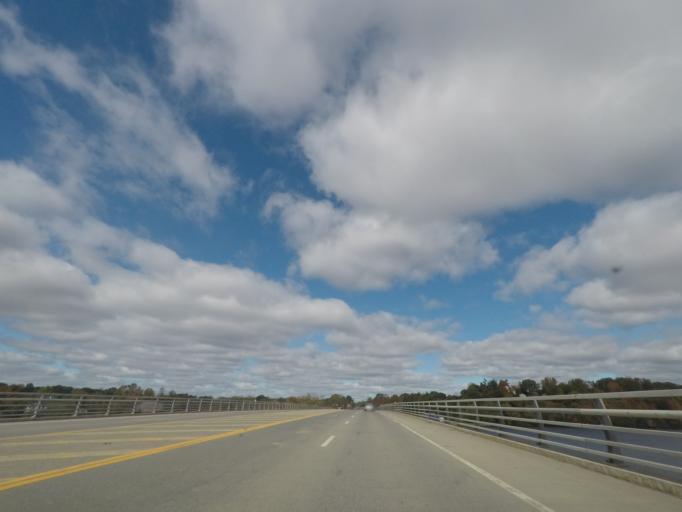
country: US
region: New York
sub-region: Albany County
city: Cohoes
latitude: 42.8199
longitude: -73.7309
